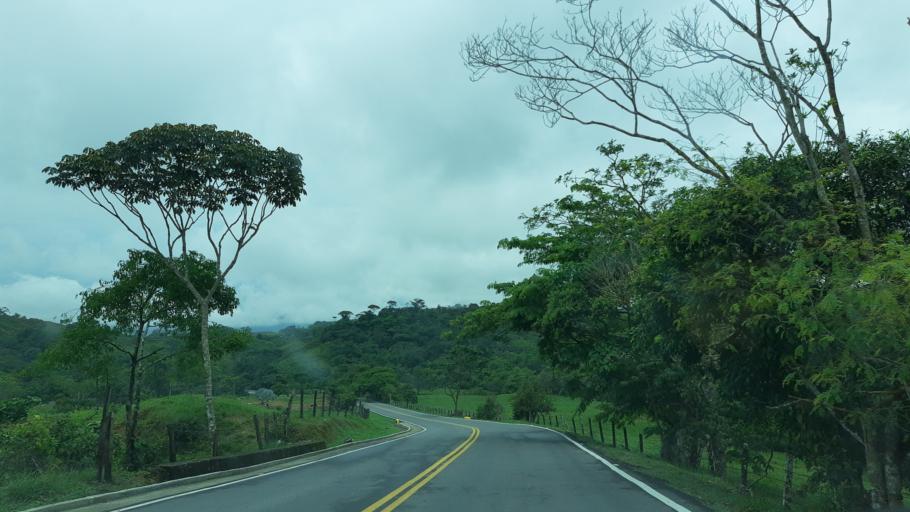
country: CO
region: Casanare
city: Sabanalarga
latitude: 4.7739
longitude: -73.0338
